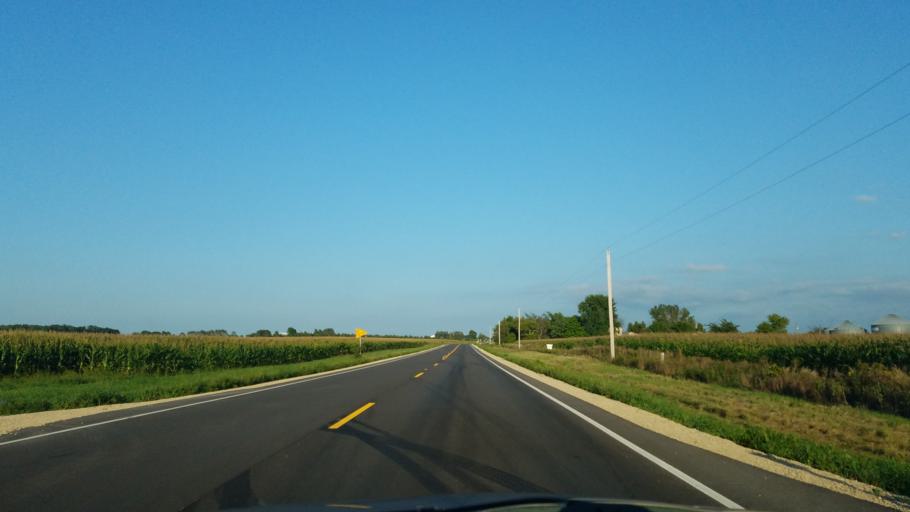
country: US
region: Wisconsin
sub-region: Saint Croix County
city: Hammond
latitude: 45.0791
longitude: -92.3854
